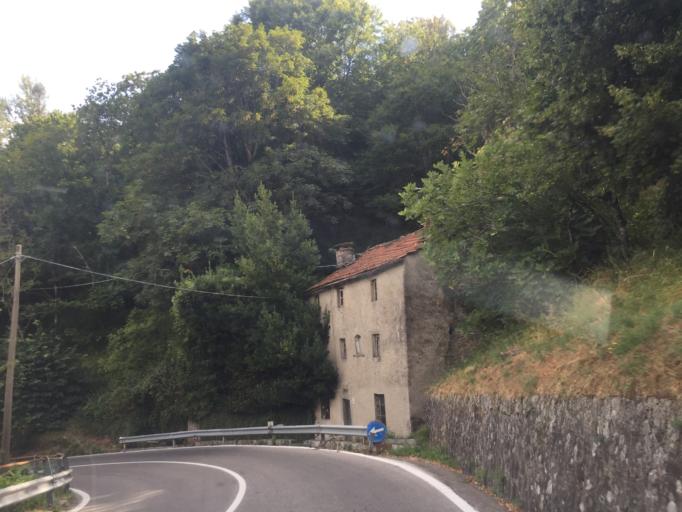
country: IT
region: Tuscany
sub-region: Provincia di Pistoia
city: Cutigliano
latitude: 44.1090
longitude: 10.7375
